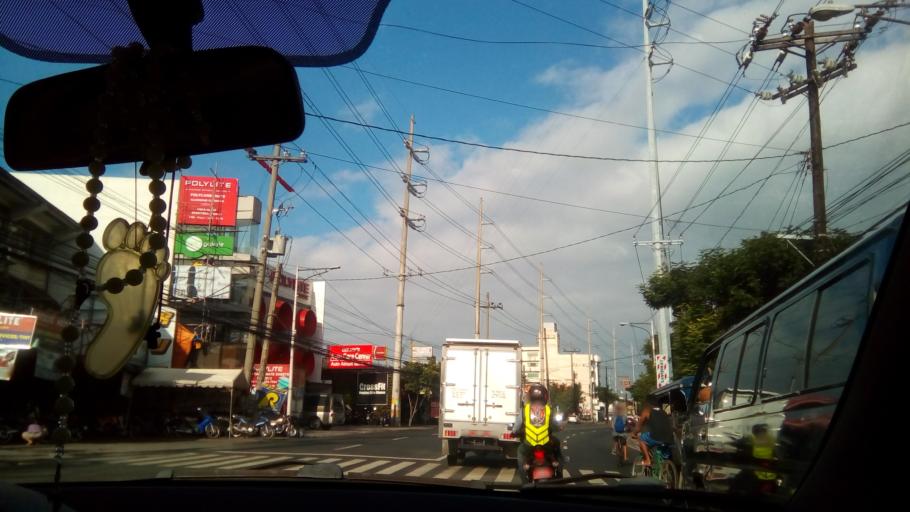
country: PH
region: Calabarzon
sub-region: Province of Rizal
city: Las Pinas
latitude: 14.4467
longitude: 120.9888
